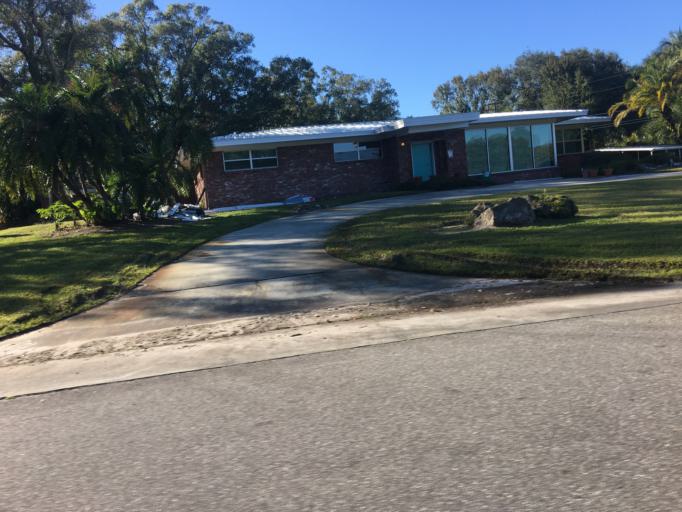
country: US
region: Florida
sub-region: Hillsborough County
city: Egypt Lake-Leto
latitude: 28.0186
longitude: -82.4651
